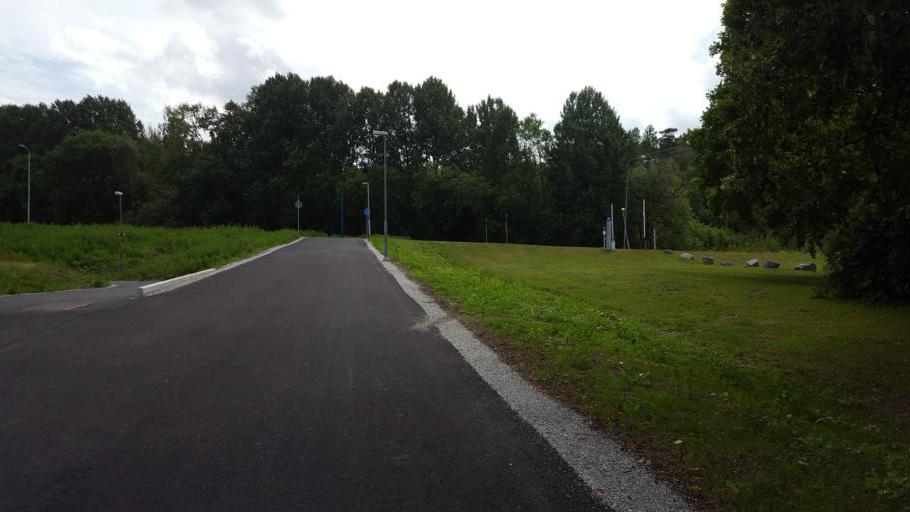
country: SE
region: Stockholm
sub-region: Upplands Vasby Kommun
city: Upplands Vaesby
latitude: 59.5074
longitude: 17.9011
